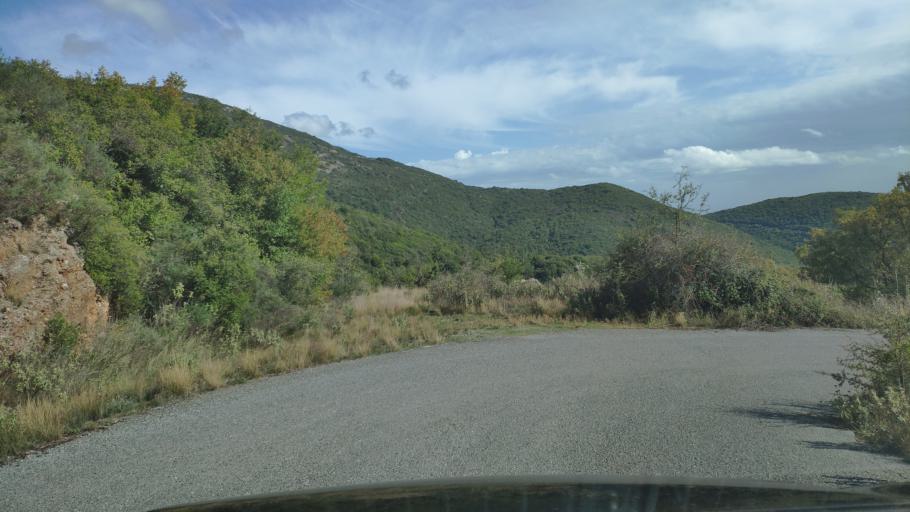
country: GR
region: Peloponnese
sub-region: Nomos Arkadias
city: Dimitsana
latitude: 37.5716
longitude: 22.0056
